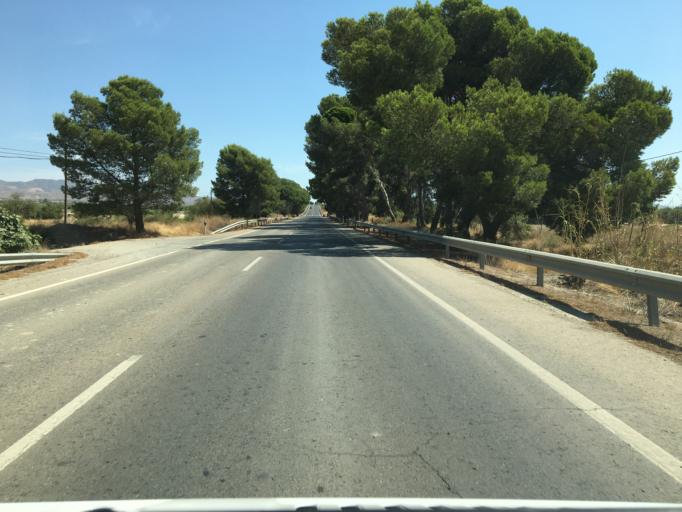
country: ES
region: Andalusia
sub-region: Provincia de Almeria
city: Huercal-Overa
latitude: 37.4226
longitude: -1.9194
